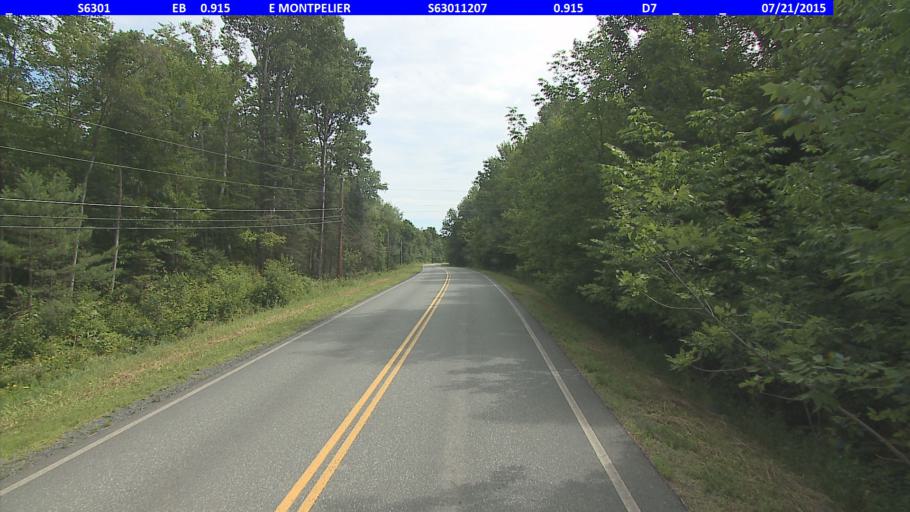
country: US
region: Vermont
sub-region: Washington County
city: Montpelier
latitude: 44.2792
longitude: -72.5378
